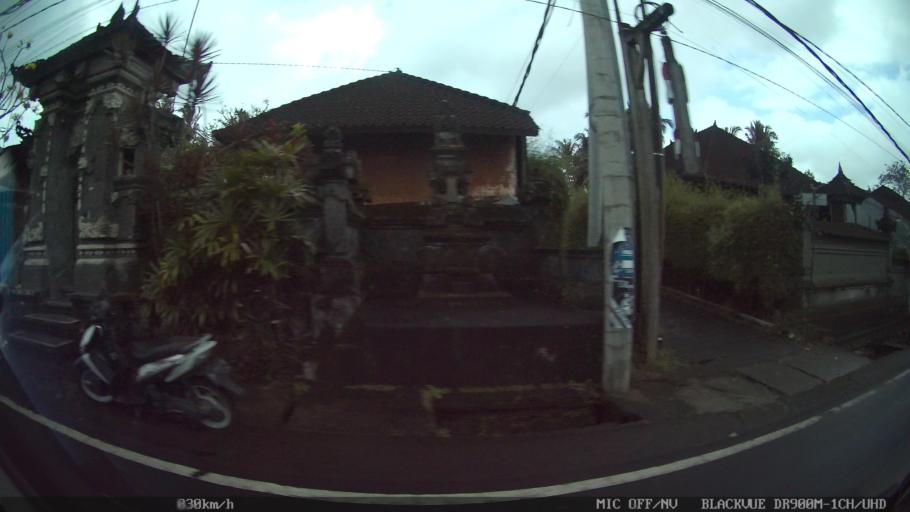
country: ID
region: Bali
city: Banjar Tebongkang
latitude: -8.5243
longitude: 115.2282
